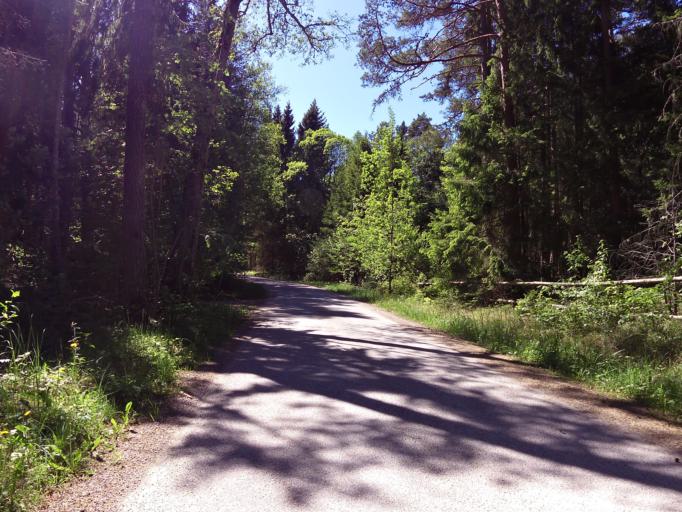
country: EE
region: Harju
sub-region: Paldiski linn
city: Paldiski
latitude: 59.2699
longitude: 23.7768
